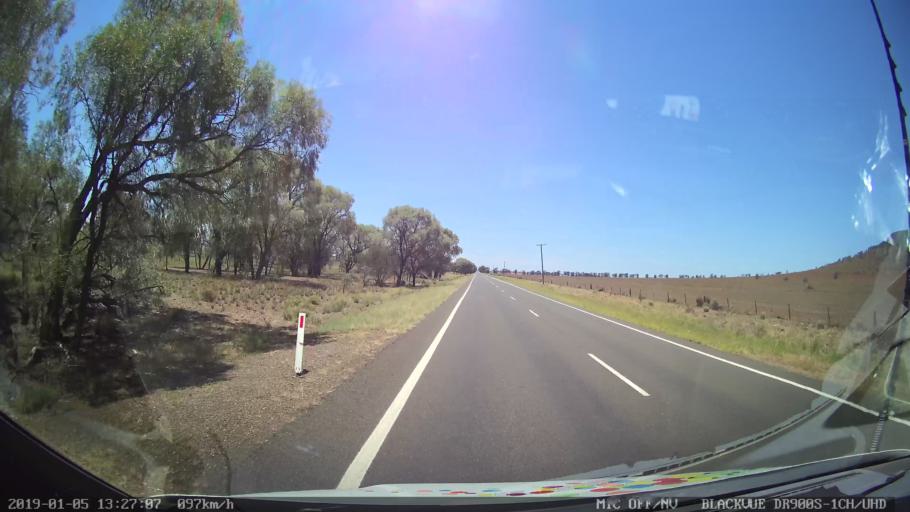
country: AU
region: New South Wales
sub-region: Gunnedah
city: Gunnedah
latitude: -31.0472
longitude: 150.0247
